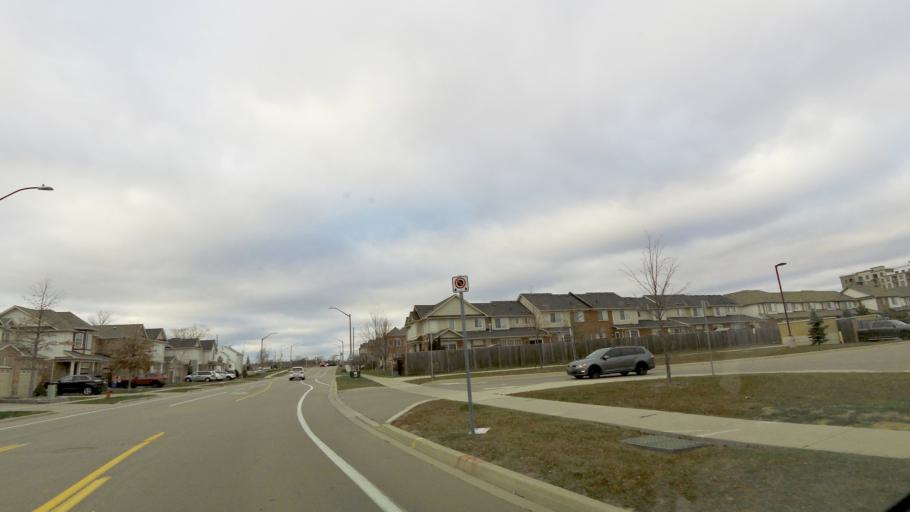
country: CA
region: Ontario
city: Burlington
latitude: 43.4314
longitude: -79.7771
